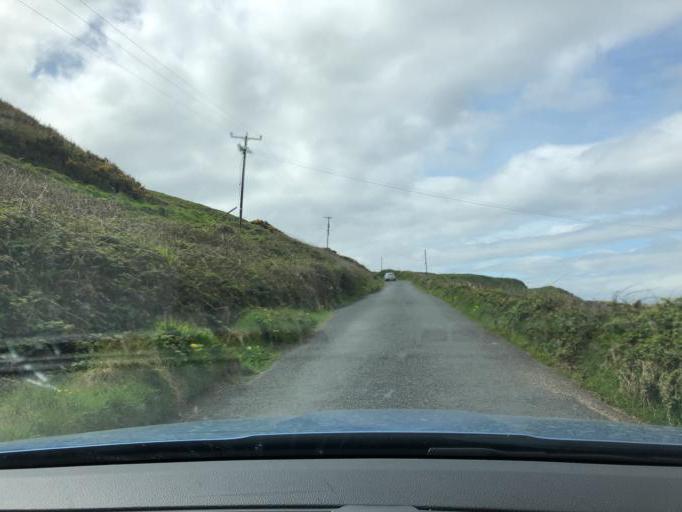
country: IE
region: Connaught
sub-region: County Galway
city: Bearna
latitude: 53.0121
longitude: -9.3850
